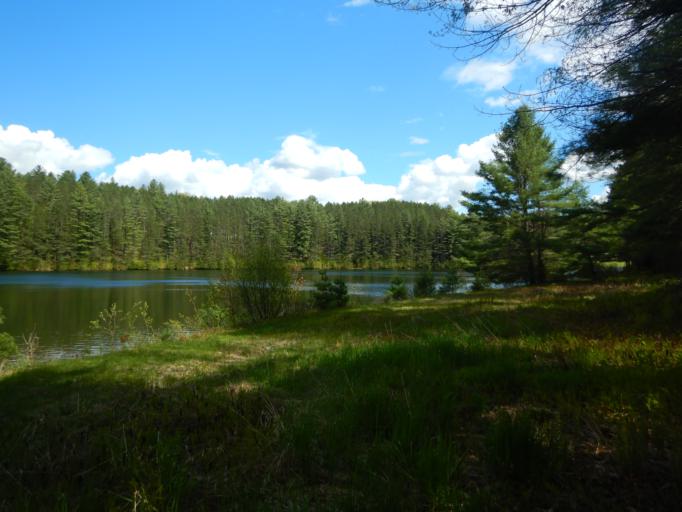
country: US
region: Vermont
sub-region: Windham County
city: West Brattleboro
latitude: 42.8854
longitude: -72.6134
